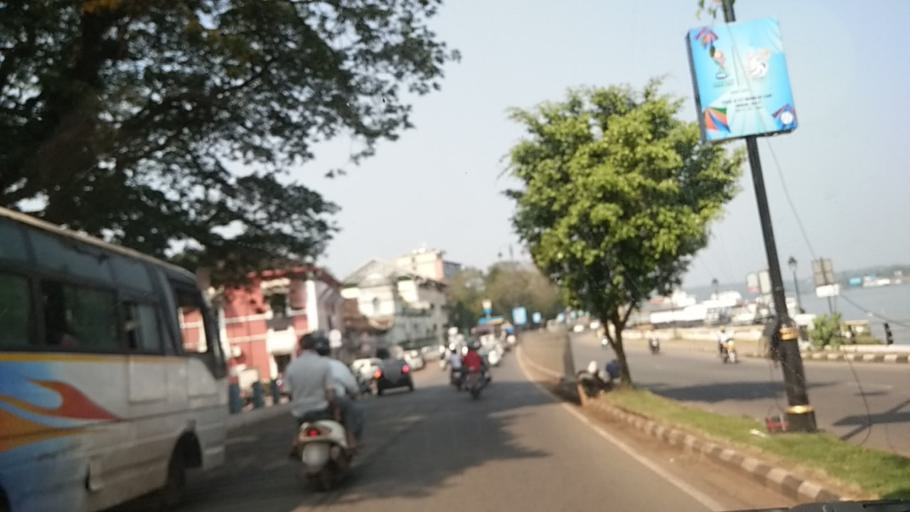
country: IN
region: Goa
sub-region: North Goa
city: Panaji
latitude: 15.4998
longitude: 73.8332
